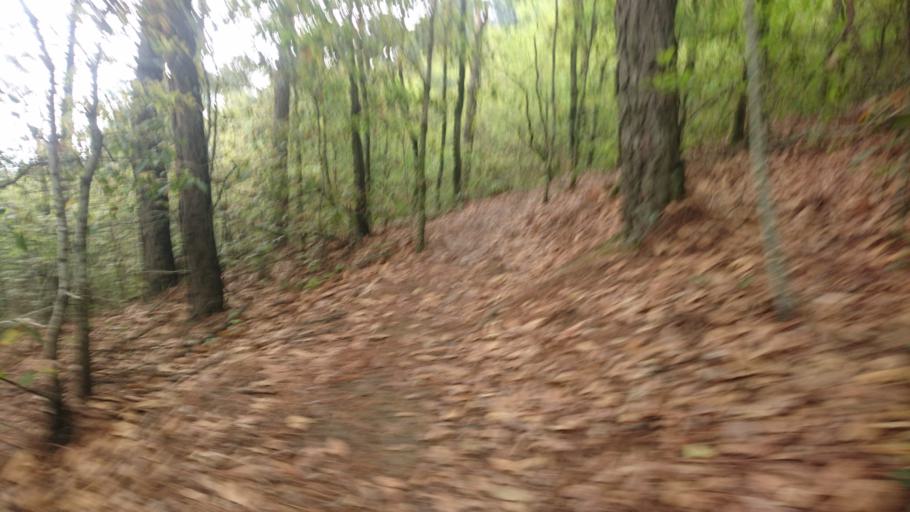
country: MX
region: Nuevo Leon
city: Garza Garcia
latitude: 25.6030
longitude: -100.3360
